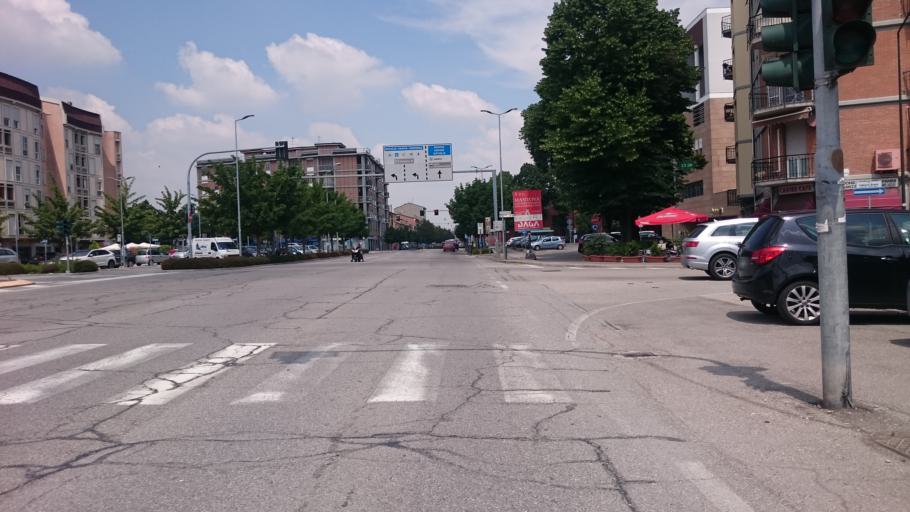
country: IT
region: Lombardy
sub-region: Provincia di Mantova
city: Mantova
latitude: 45.1465
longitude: 10.7956
